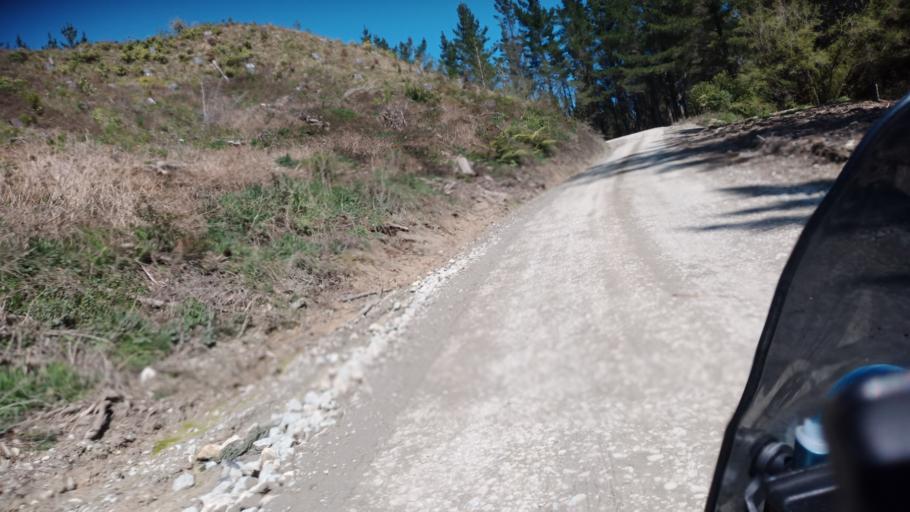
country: NZ
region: Gisborne
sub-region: Gisborne District
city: Gisborne
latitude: -38.8978
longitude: 177.8014
